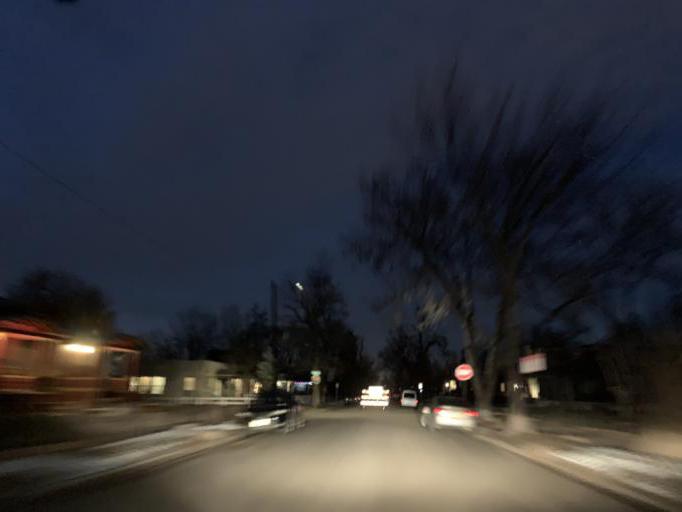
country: US
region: Colorado
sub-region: Jefferson County
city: Edgewater
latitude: 39.7744
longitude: -105.0520
